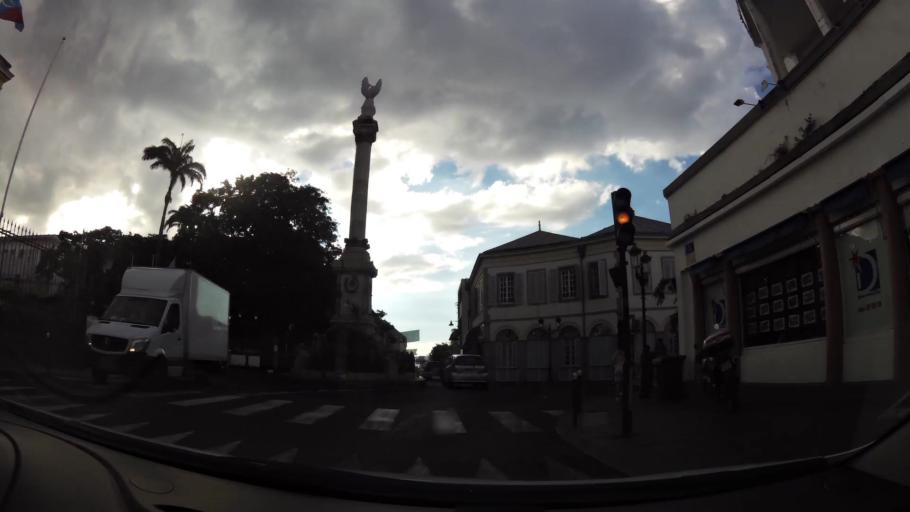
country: RE
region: Reunion
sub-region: Reunion
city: Saint-Denis
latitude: -20.8786
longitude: 55.4486
